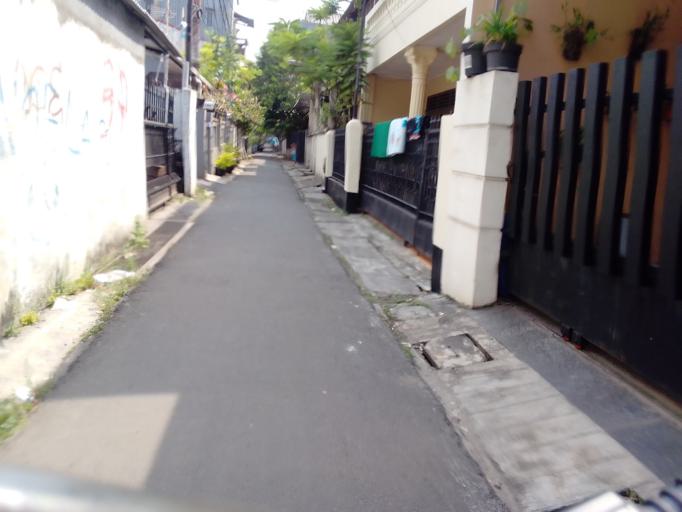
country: ID
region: Jakarta Raya
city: Jakarta
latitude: -6.2102
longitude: 106.8108
